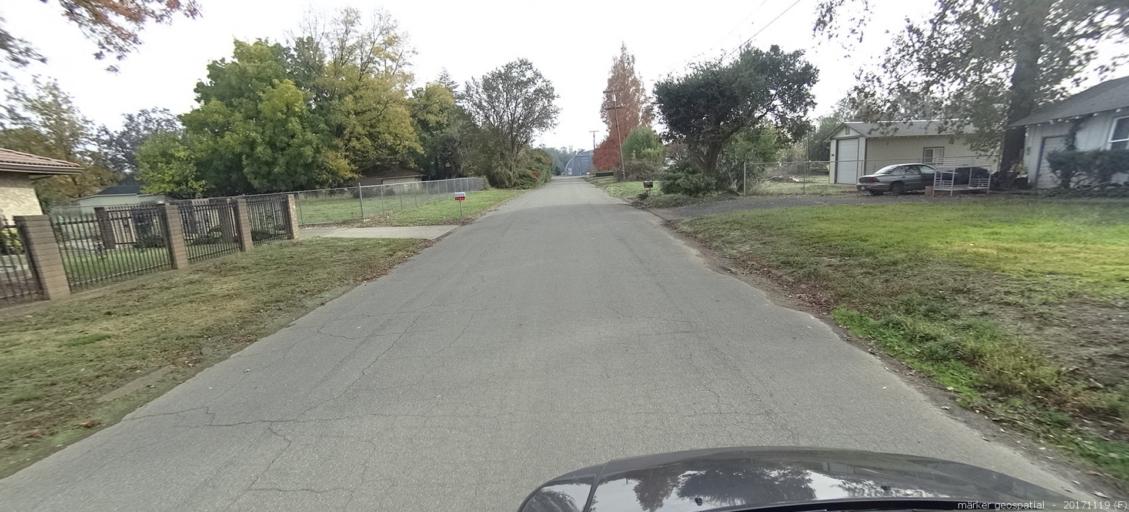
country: US
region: California
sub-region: Shasta County
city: Redding
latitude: 40.5243
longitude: -122.3412
